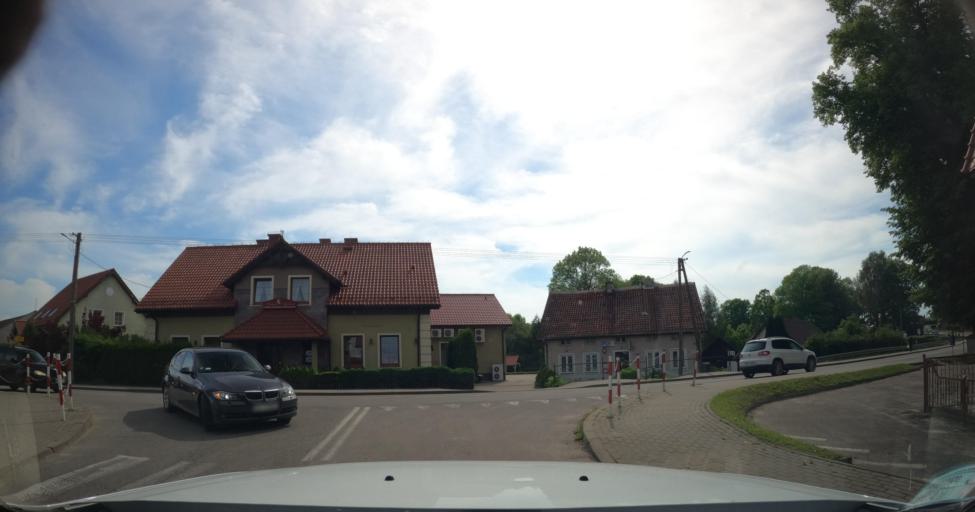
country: PL
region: Warmian-Masurian Voivodeship
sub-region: Powiat lidzbarski
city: Lubomino
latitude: 54.0668
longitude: 20.2389
